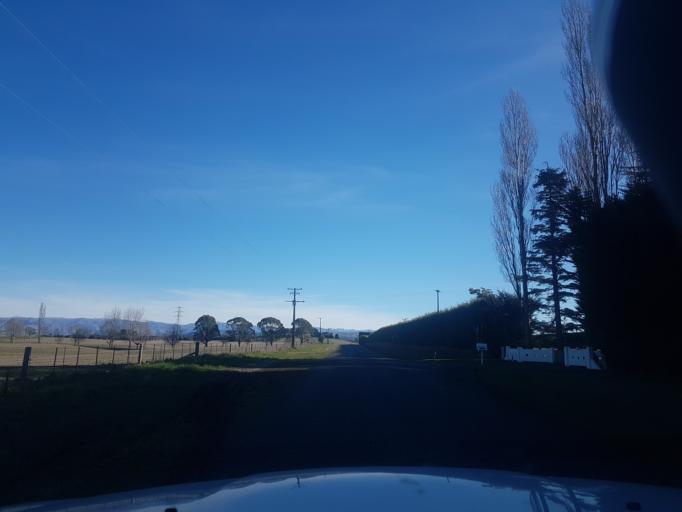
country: NZ
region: Canterbury
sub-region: Timaru District
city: Pleasant Point
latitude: -44.2519
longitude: 171.0541
